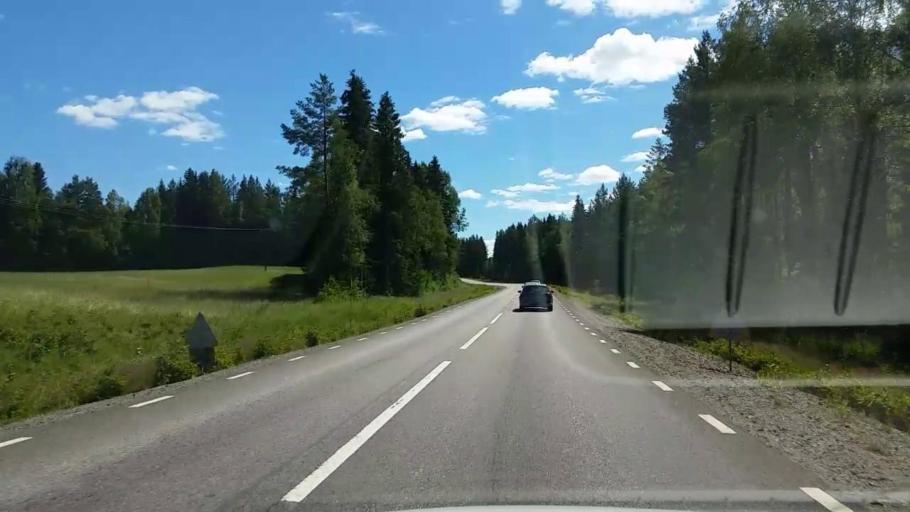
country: SE
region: Gaevleborg
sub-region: Ovanakers Kommun
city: Edsbyn
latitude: 61.1971
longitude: 15.8738
